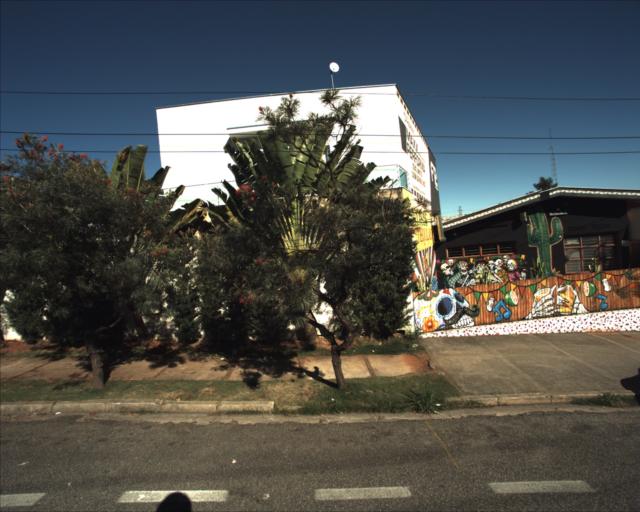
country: BR
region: Sao Paulo
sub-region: Sorocaba
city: Sorocaba
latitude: -23.5116
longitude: -47.4935
